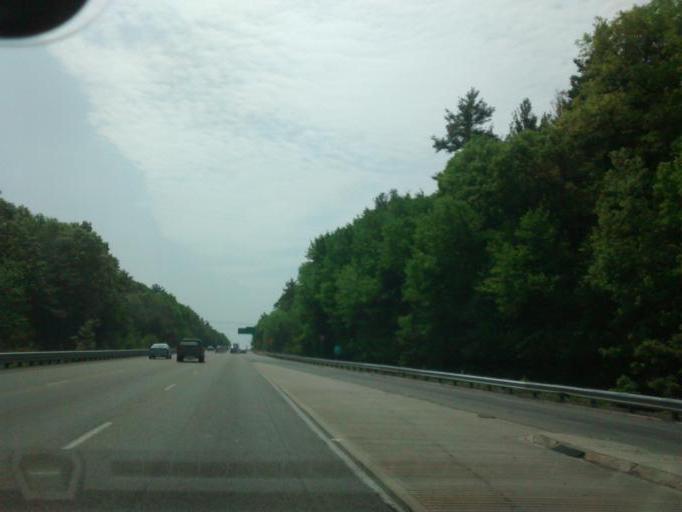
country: US
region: Massachusetts
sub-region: Middlesex County
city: Hopkinton
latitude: 42.2153
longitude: -71.5473
